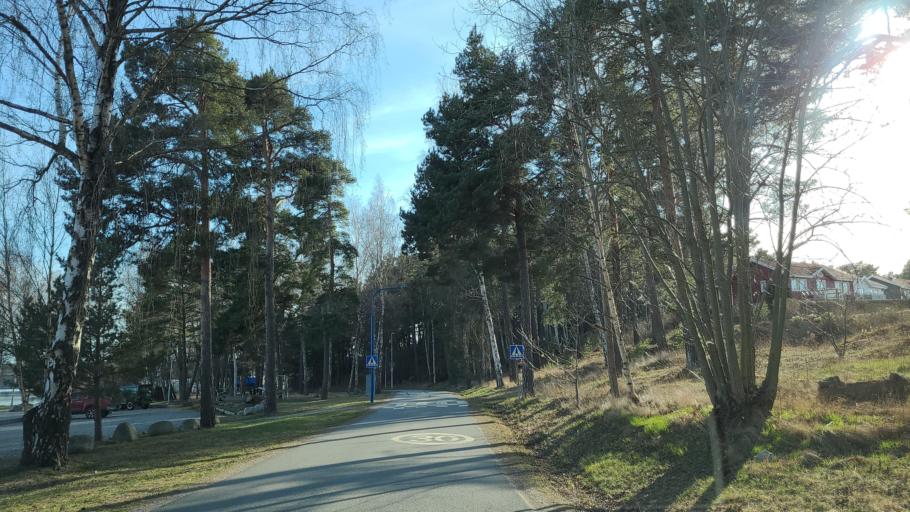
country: SE
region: Stockholm
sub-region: Ekero Kommun
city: Ekeroe
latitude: 59.2688
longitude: 17.7815
